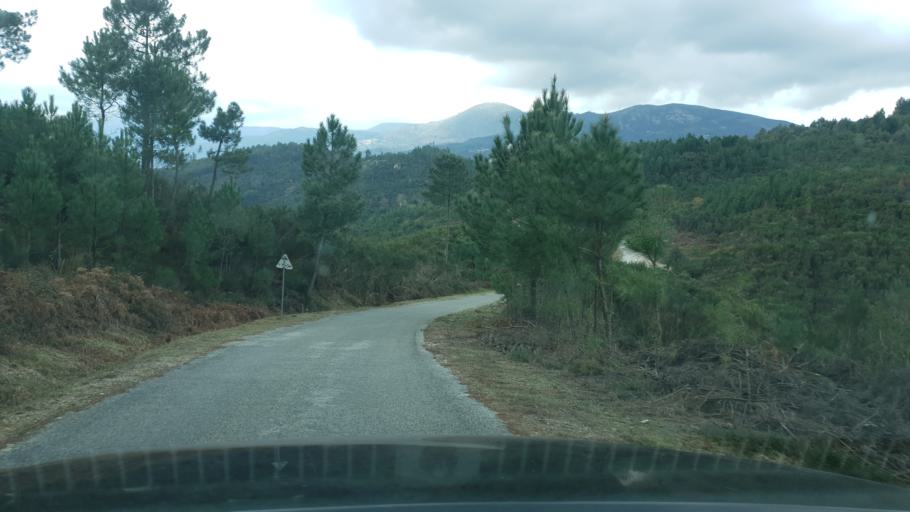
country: PT
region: Viseu
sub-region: Castro Daire
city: Castro Daire
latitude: 40.8792
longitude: -7.9971
